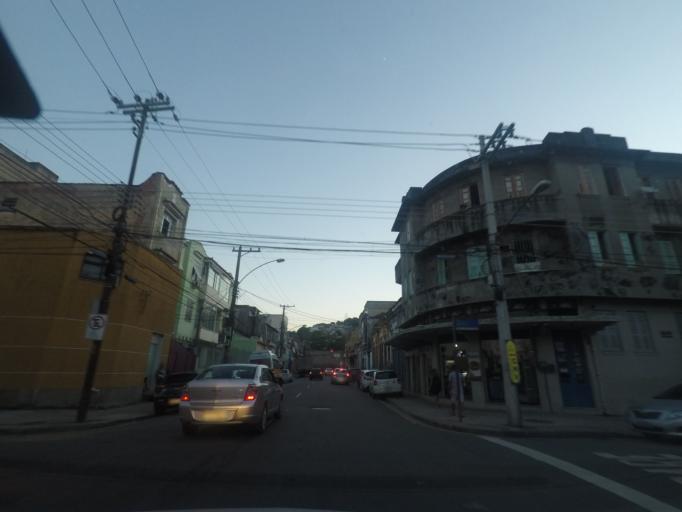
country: BR
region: Rio de Janeiro
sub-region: Rio De Janeiro
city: Rio de Janeiro
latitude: -22.9131
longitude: -43.1995
